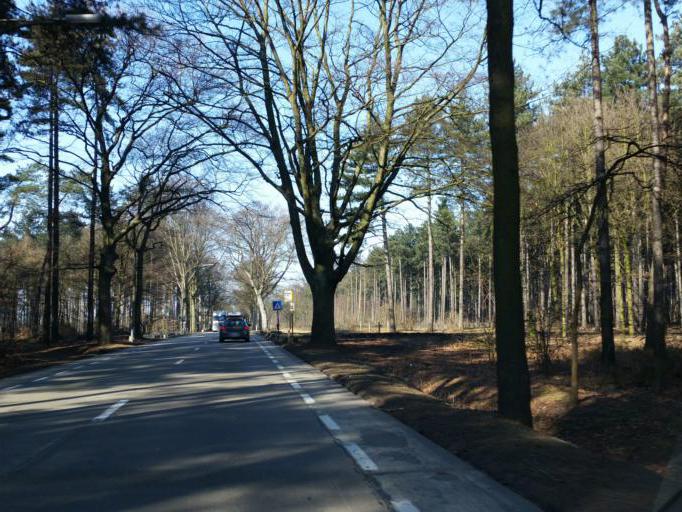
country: BE
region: Flanders
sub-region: Provincie Oost-Vlaanderen
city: Zelzate
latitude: 51.1810
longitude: 3.8383
